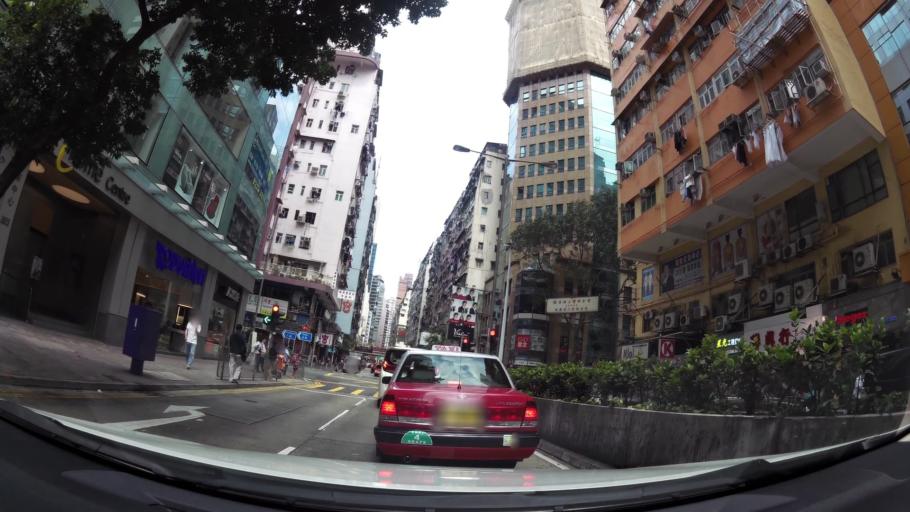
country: HK
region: Wanchai
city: Wan Chai
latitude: 22.2792
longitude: 114.1793
